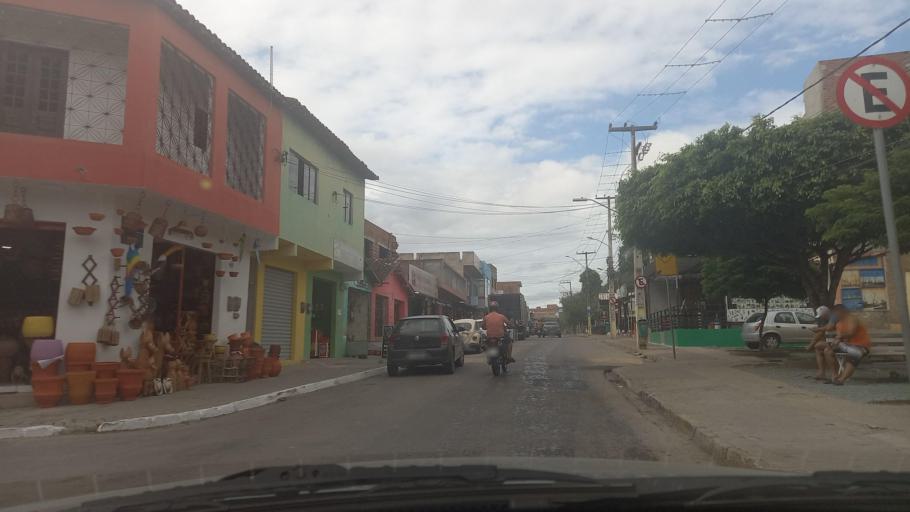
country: BR
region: Pernambuco
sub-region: Caruaru
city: Caruaru
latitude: -8.2917
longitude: -36.0304
